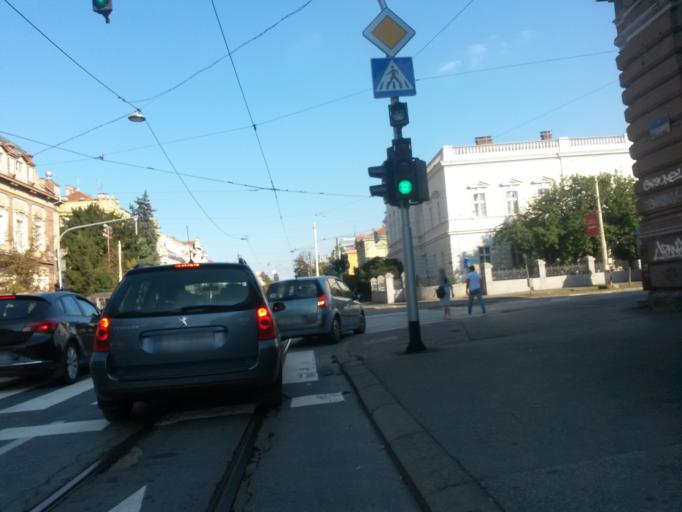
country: HR
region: Osjecko-Baranjska
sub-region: Grad Osijek
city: Osijek
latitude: 45.5609
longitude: 18.6820
